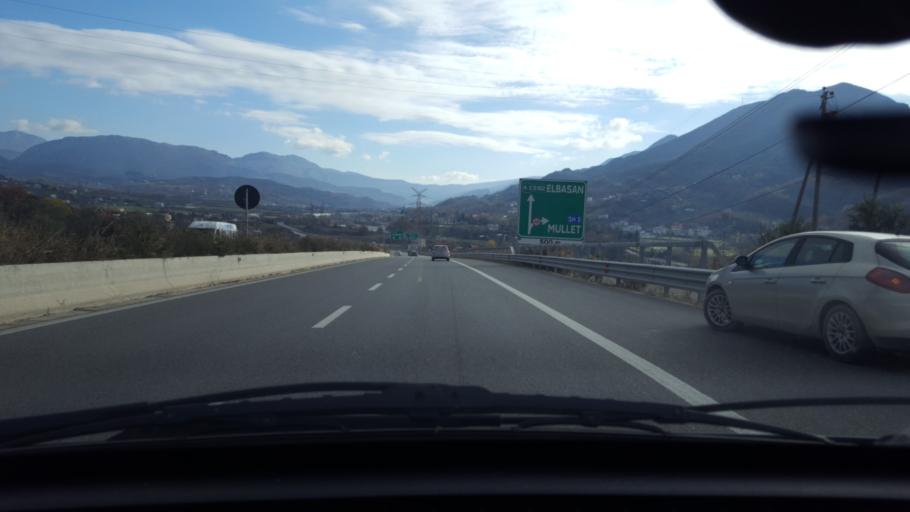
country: AL
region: Tirane
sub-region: Rrethi i Tiranes
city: Petrele
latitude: 41.2671
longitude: 19.8657
